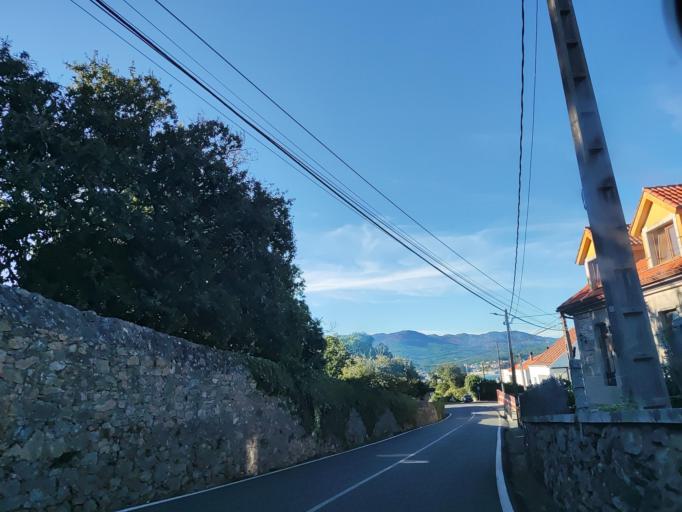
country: ES
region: Galicia
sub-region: Provincia da Coruna
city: Boiro
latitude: 42.5932
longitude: -8.9297
